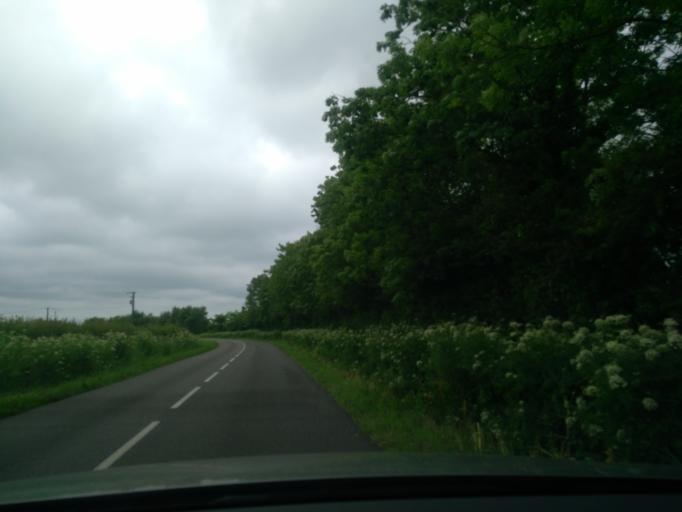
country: FR
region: Lower Normandy
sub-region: Departement de la Manche
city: Sainte-Mere-Eglise
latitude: 49.4589
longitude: -1.2629
